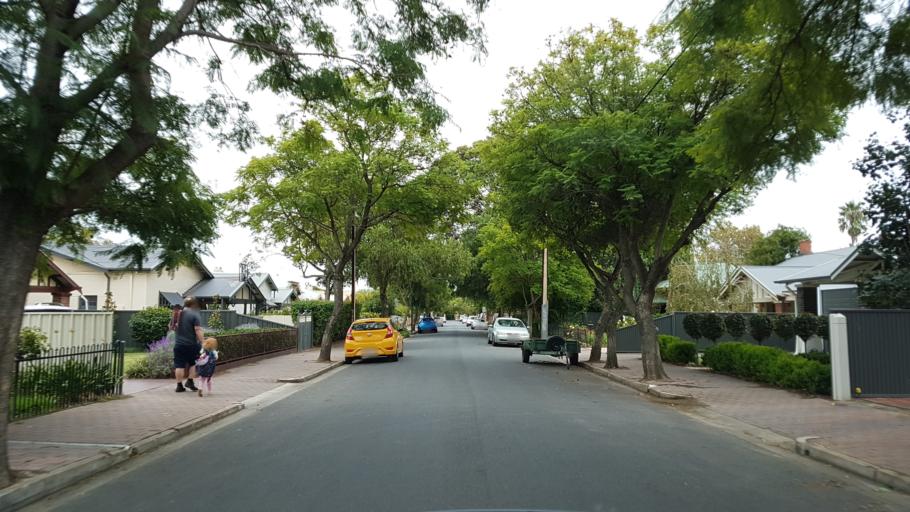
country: AU
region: South Australia
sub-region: Unley
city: Forestville
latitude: -34.9612
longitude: 138.5788
